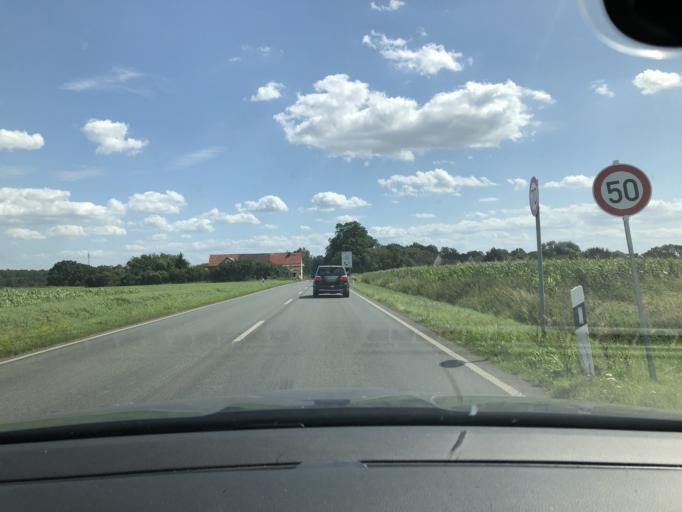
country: DE
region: Brandenburg
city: Neuruppin
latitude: 52.9292
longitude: 12.8945
